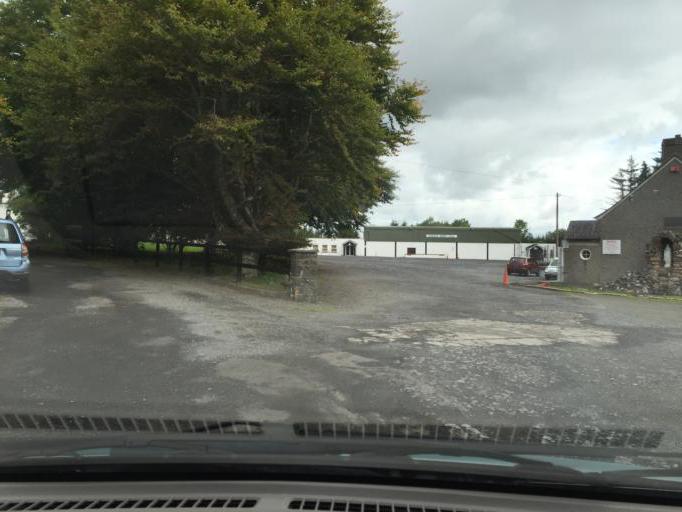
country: IE
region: Connaught
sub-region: Sligo
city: Tobercurry
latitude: 54.0387
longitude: -8.8168
